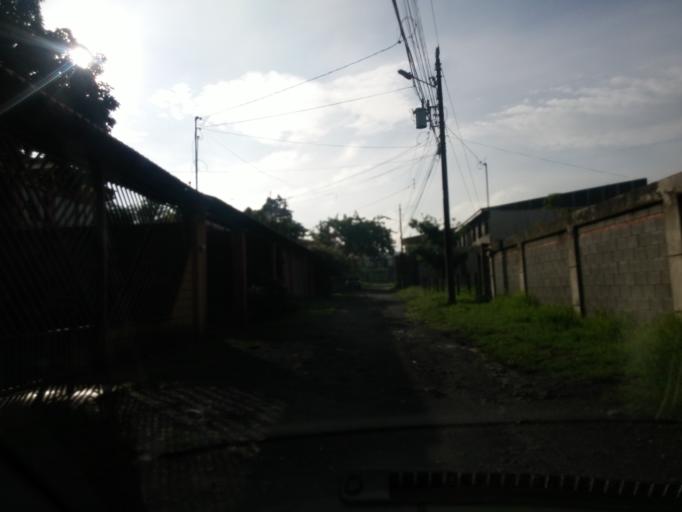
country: CR
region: Heredia
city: Llorente
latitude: 9.9962
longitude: -84.1516
